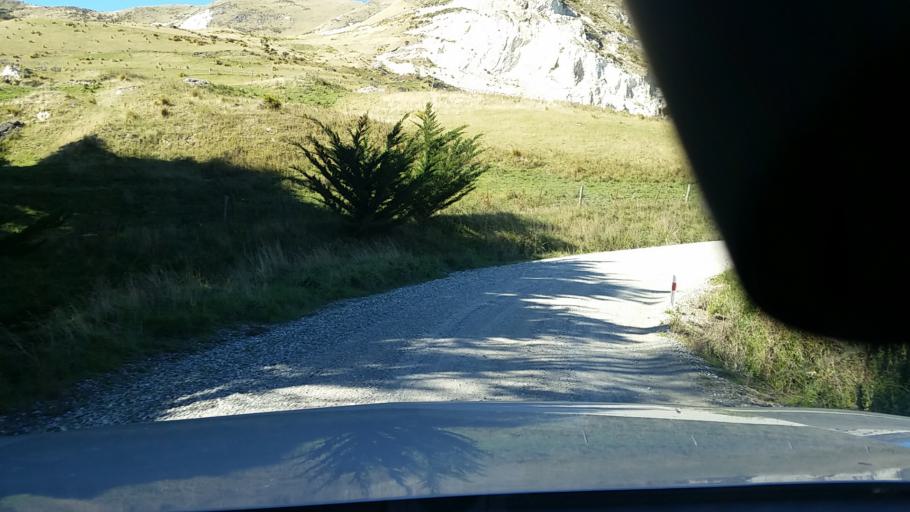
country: NZ
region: Marlborough
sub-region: Marlborough District
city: Blenheim
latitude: -41.8319
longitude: 174.1747
